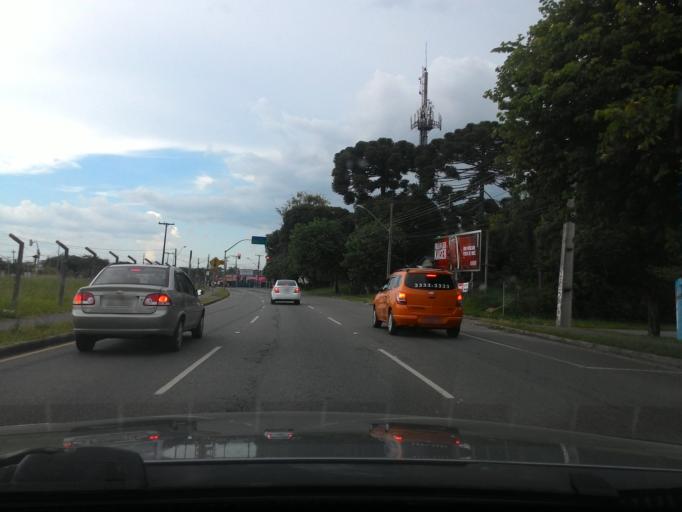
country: BR
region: Parana
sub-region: Pinhais
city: Pinhais
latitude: -25.4442
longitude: -49.2094
